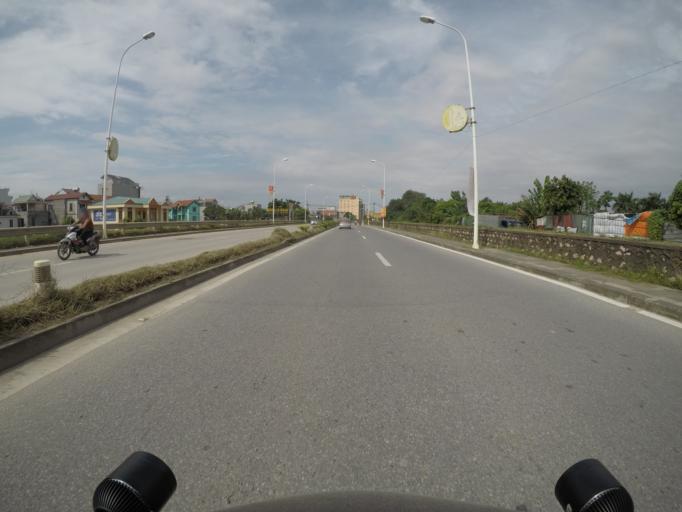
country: VN
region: Ha Noi
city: Tay Ho
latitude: 21.0902
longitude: 105.7926
